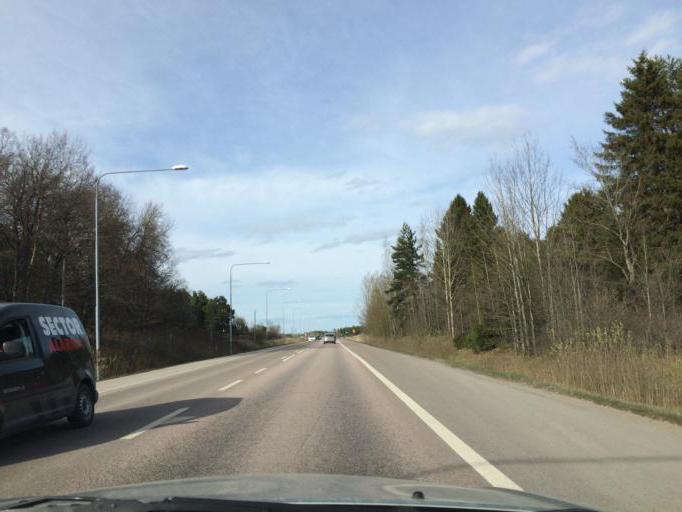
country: SE
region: Soedermanland
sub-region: Eskilstuna Kommun
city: Torshalla
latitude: 59.3979
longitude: 16.4708
